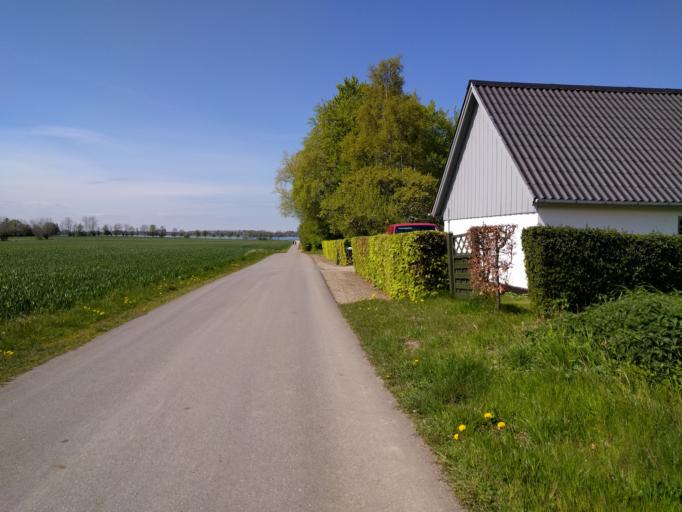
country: DK
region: South Denmark
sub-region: Kerteminde Kommune
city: Munkebo
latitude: 55.4459
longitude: 10.5877
